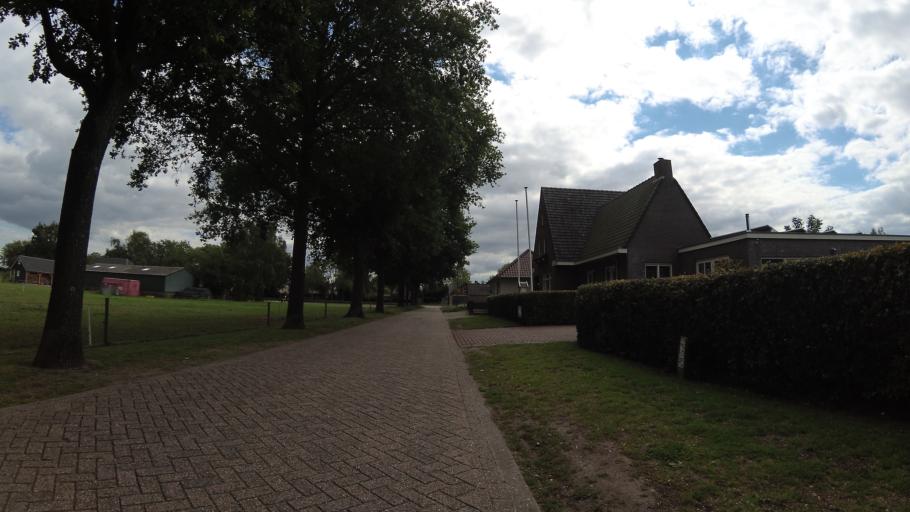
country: NL
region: North Brabant
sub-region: Gemeente Dongen
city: Dongen
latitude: 51.6340
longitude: 4.9179
